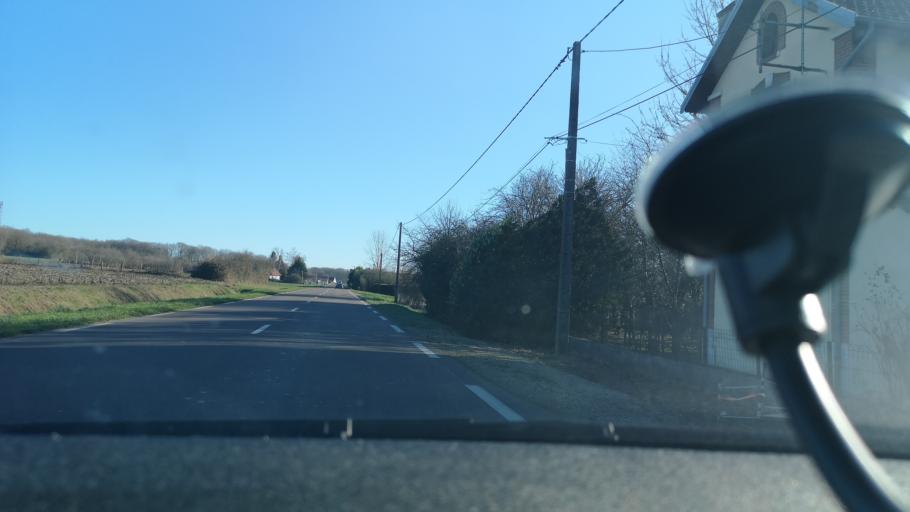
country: FR
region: Bourgogne
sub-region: Departement de Saone-et-Loire
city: Ouroux-sur-Saone
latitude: 46.7721
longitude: 4.9706
